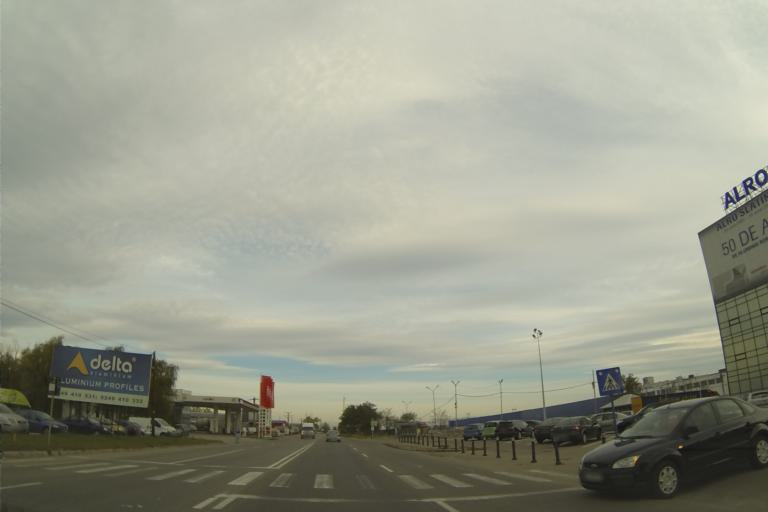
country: RO
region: Olt
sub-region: Municipiul Slatina
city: Slatina
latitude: 44.4475
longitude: 24.3845
